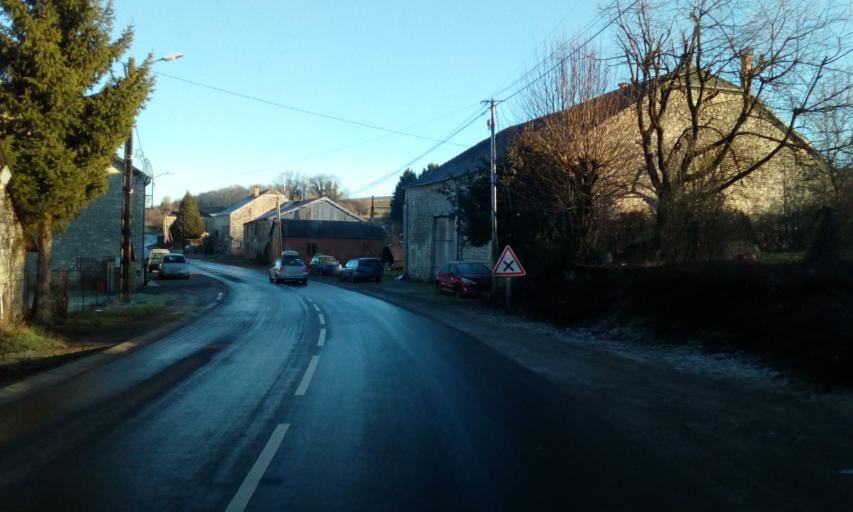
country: FR
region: Champagne-Ardenne
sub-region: Departement des Ardennes
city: Rimogne
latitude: 49.7774
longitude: 4.3967
